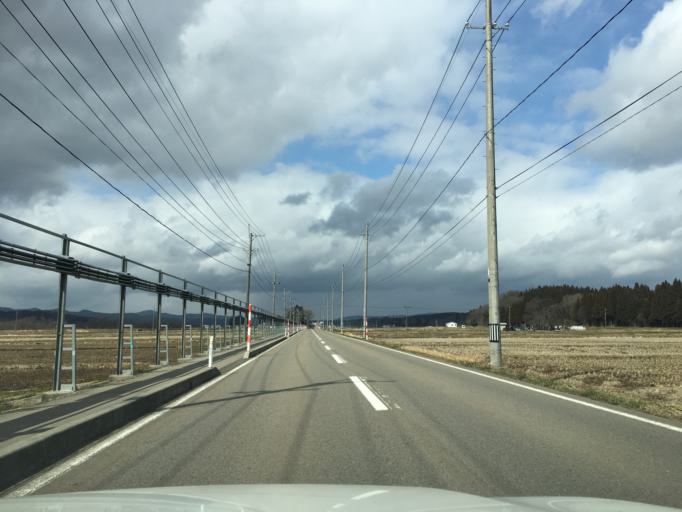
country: JP
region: Akita
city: Takanosu
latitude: 40.1297
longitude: 140.3612
